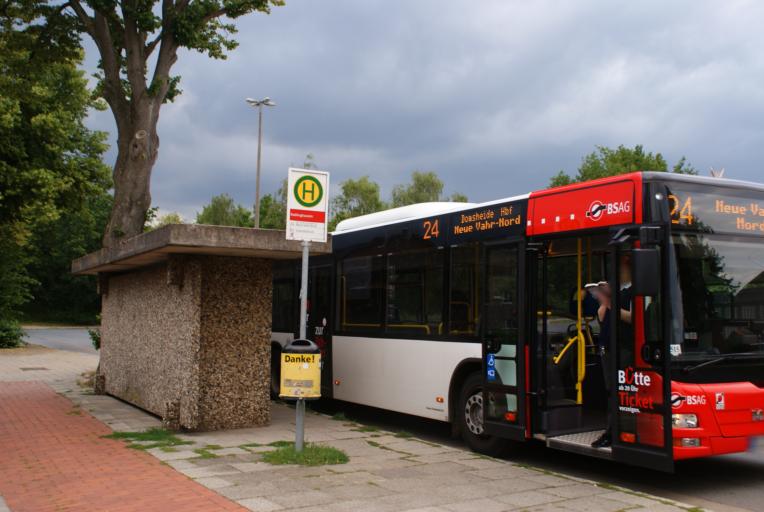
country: DE
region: Lower Saxony
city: Stuhr
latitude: 53.0959
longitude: 8.7462
